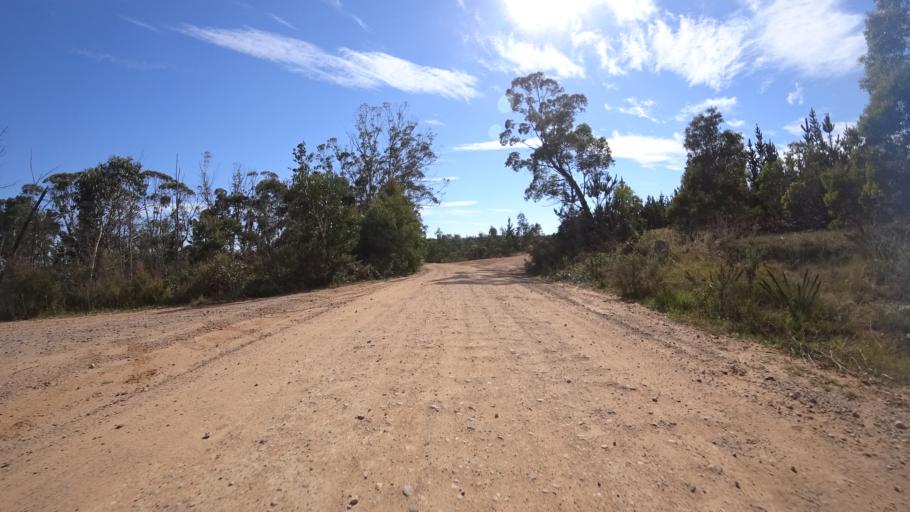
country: AU
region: New South Wales
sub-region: Lithgow
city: Lithgow
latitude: -33.3579
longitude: 150.2518
